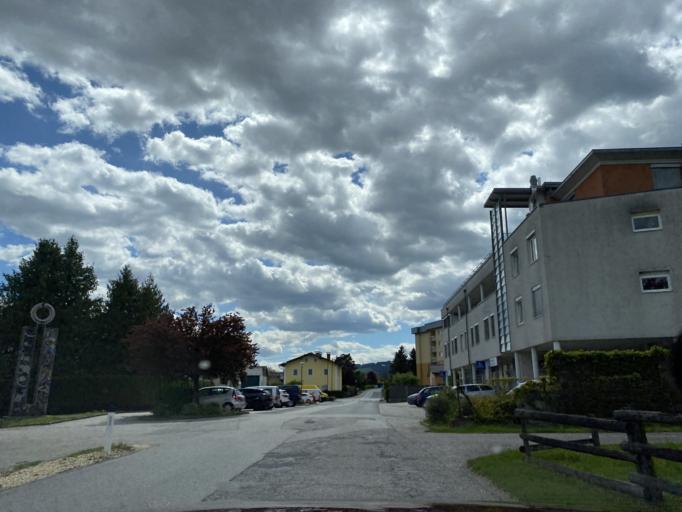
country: AT
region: Carinthia
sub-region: Politischer Bezirk Wolfsberg
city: Wolfsberg
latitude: 46.8298
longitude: 14.8345
